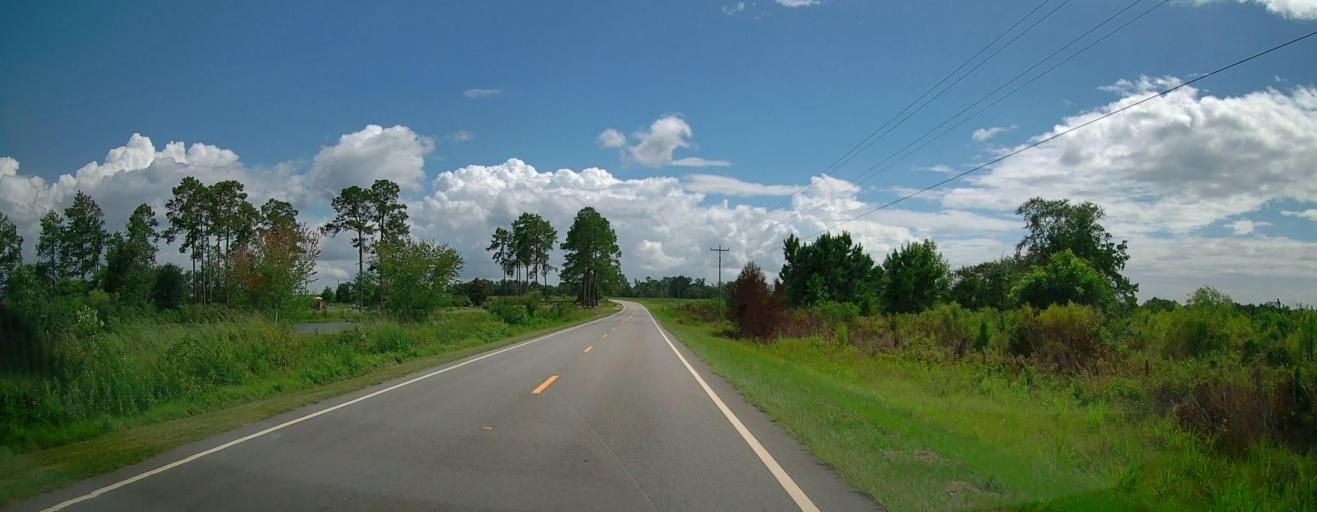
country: US
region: Georgia
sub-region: Irwin County
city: Ocilla
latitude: 31.6082
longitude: -83.1659
